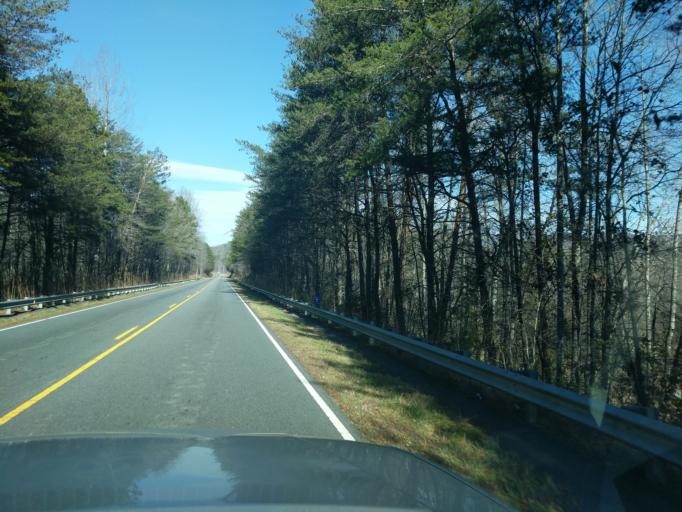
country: US
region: North Carolina
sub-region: Rutherford County
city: Rutherfordton
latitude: 35.5054
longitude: -81.9756
